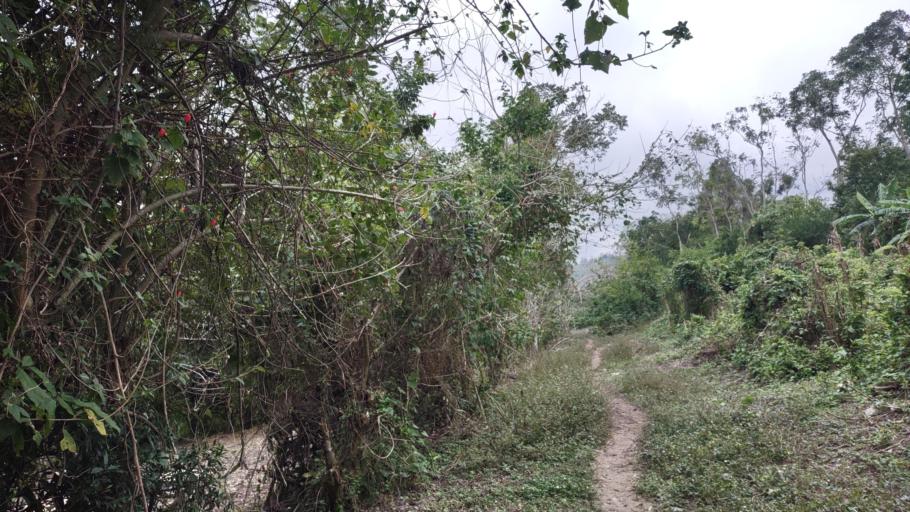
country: MX
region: Veracruz
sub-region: Coatzintla
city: Manuel Maria Contreras
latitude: 20.4112
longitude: -97.4551
